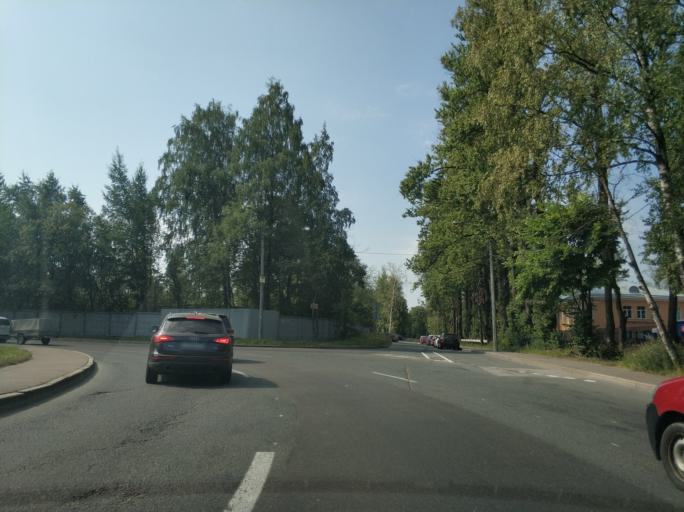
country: RU
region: St.-Petersburg
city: Krasnogvargeisky
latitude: 59.9777
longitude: 30.4995
